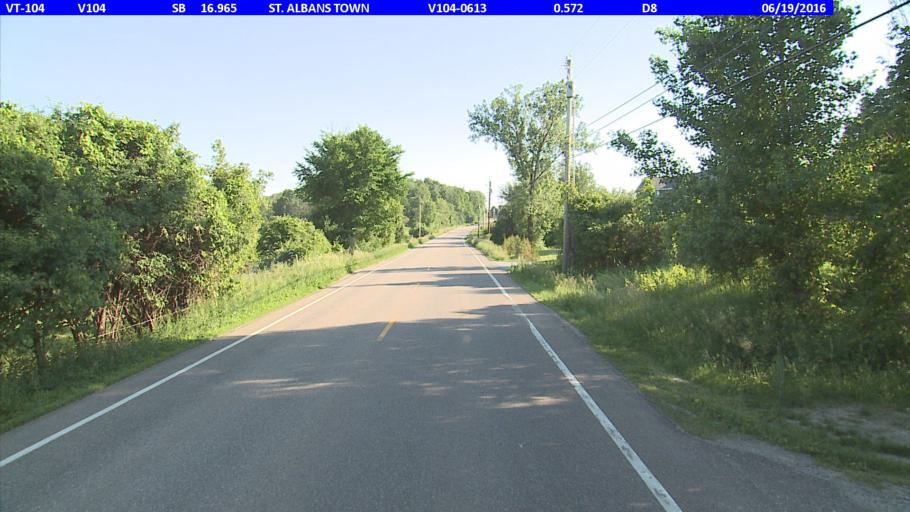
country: US
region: Vermont
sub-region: Franklin County
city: Saint Albans
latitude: 44.7820
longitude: -73.0782
